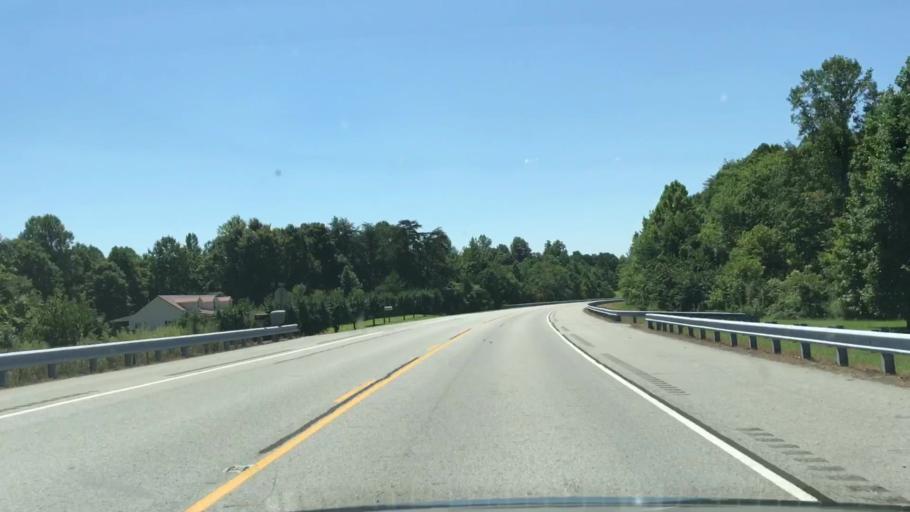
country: US
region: Tennessee
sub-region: Clay County
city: Celina
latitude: 36.5850
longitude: -85.4422
